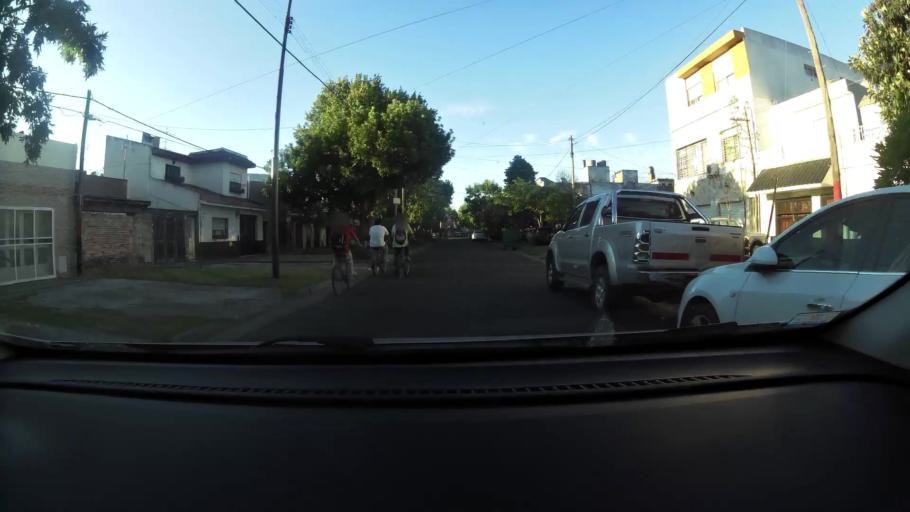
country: AR
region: Santa Fe
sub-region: Departamento de Rosario
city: Rosario
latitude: -32.9683
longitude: -60.6711
